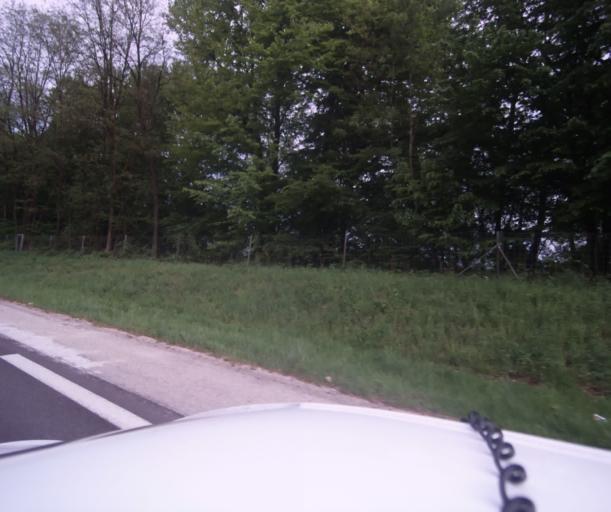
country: FR
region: Franche-Comte
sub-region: Departement du Doubs
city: Franois
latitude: 47.2129
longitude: 5.9300
